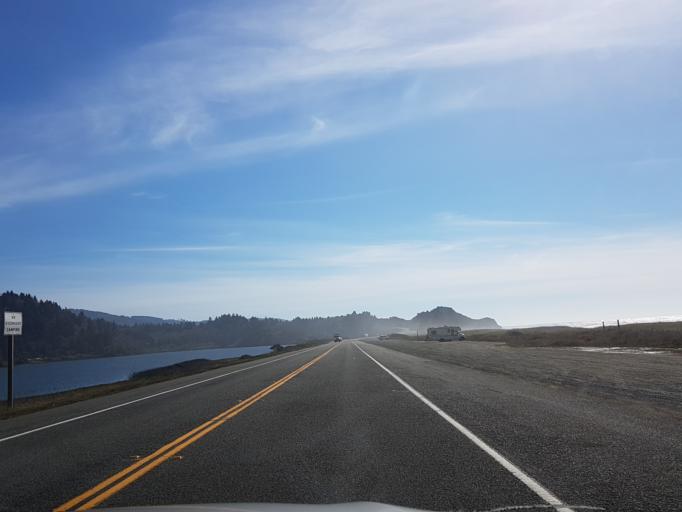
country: US
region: California
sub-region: Humboldt County
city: Westhaven-Moonstone
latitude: 41.2777
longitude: -124.0941
